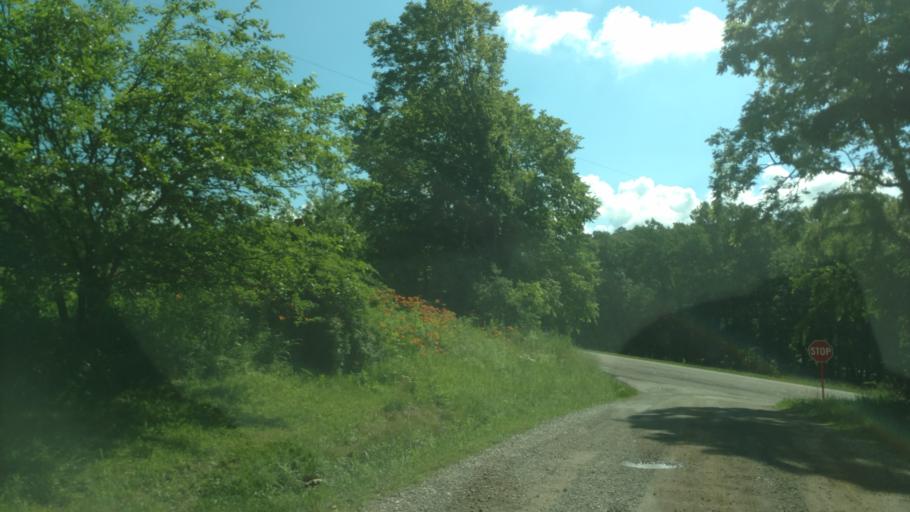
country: US
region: Ohio
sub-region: Knox County
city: Danville
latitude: 40.5188
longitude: -82.3242
